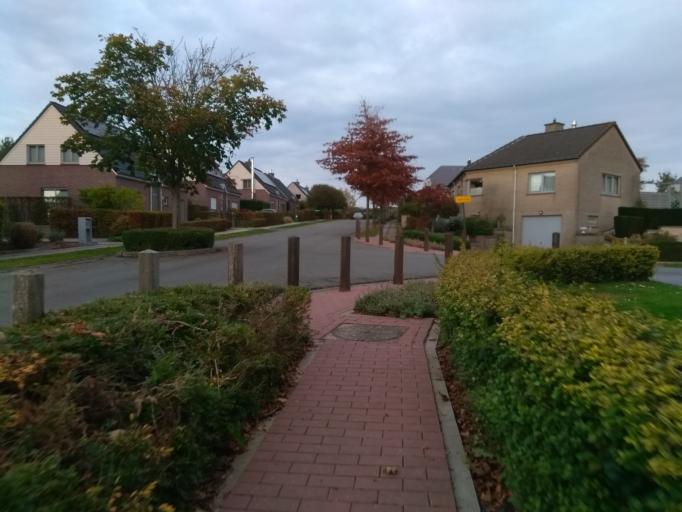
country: BE
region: Flanders
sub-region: Provincie Oost-Vlaanderen
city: Oosterzele
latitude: 50.9217
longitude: 3.7969
